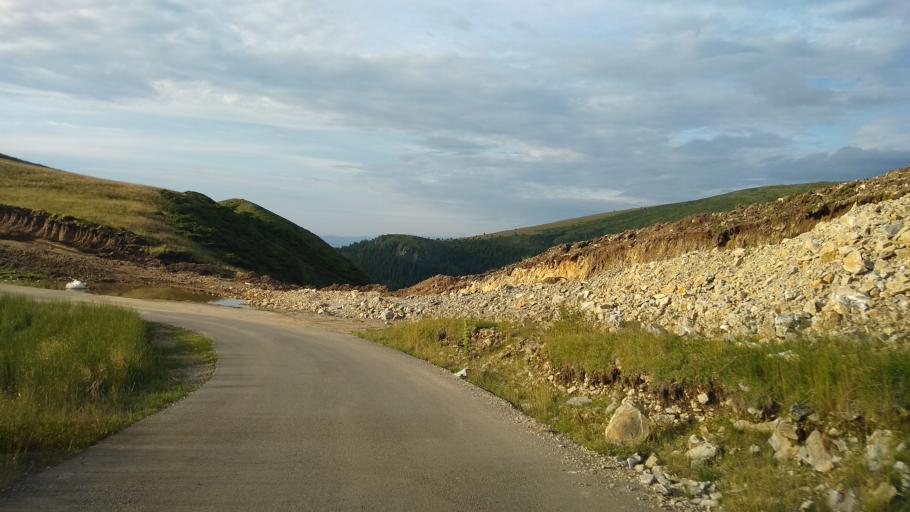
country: RO
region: Hunedoara
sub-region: Municipiul  Vulcan
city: Jiu-Paroseni
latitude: 45.3091
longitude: 23.3125
